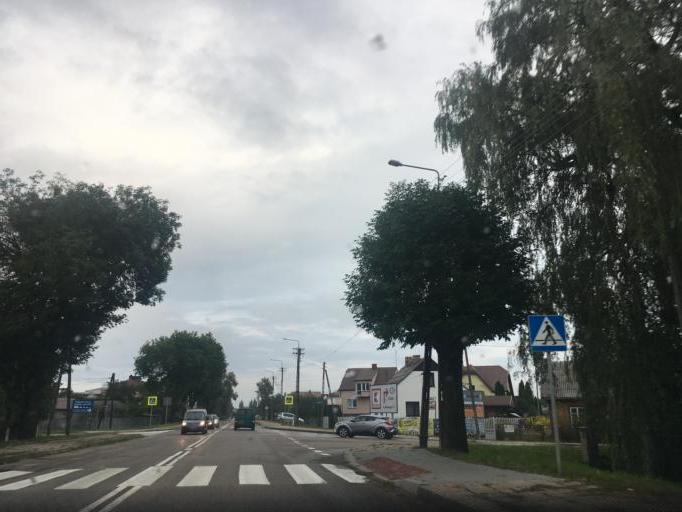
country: PL
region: Podlasie
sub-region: Powiat hajnowski
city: Hajnowka
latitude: 52.7412
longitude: 23.5665
